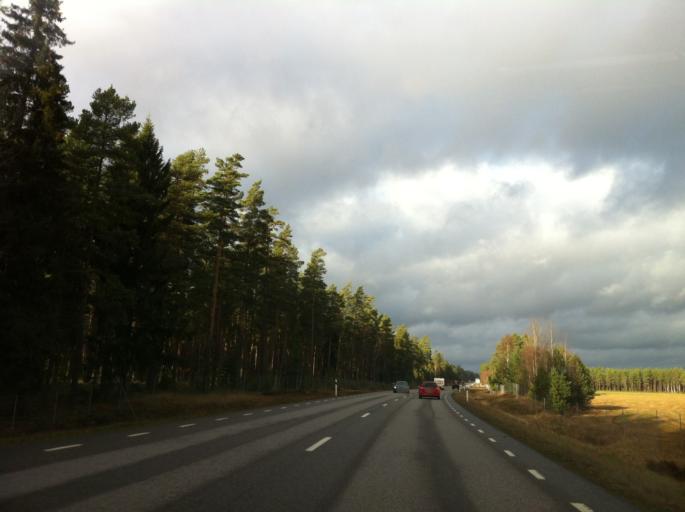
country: SE
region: Kalmar
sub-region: Vimmerby Kommun
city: Vimmerby
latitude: 57.6181
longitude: 15.8443
